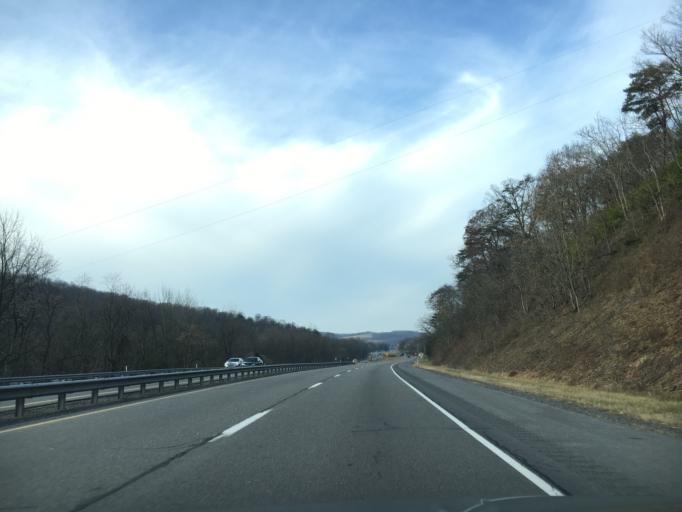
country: US
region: Pennsylvania
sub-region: Montour County
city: Danville
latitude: 40.9784
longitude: -76.6236
